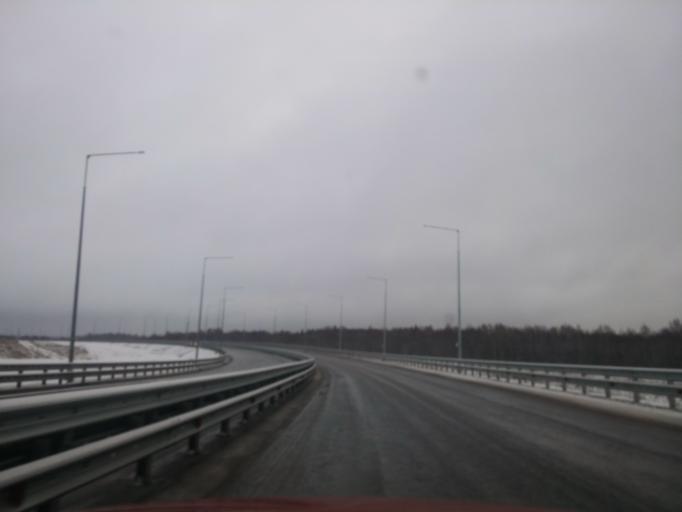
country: RU
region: Tverskaya
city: Likhoslavl'
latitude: 56.9597
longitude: 35.4828
